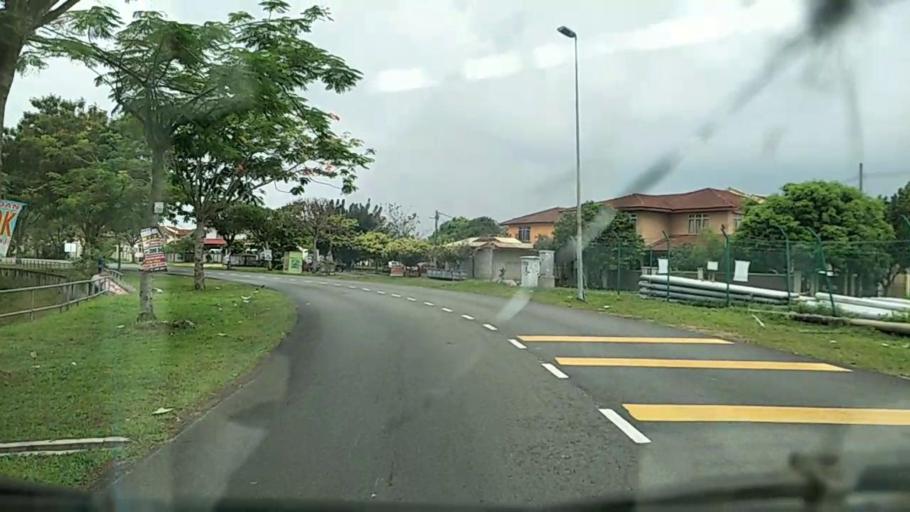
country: MY
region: Putrajaya
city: Putrajaya
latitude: 2.9461
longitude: 101.6196
